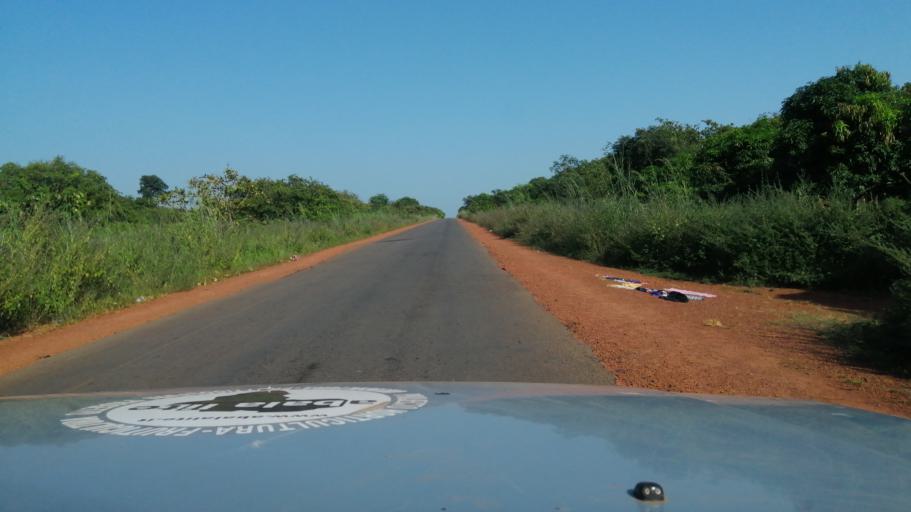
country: GW
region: Bissau
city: Bissau
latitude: 11.9588
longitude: -15.5257
